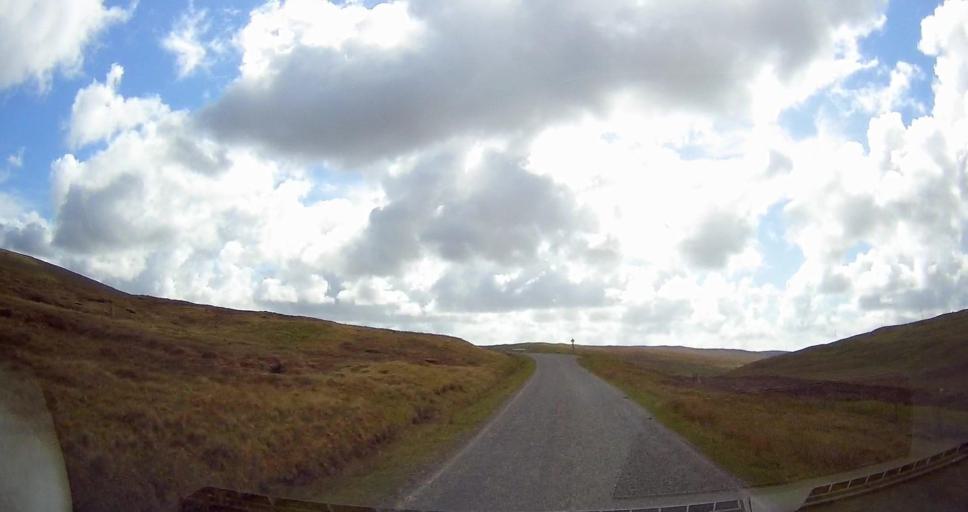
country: GB
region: Scotland
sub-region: Shetland Islands
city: Lerwick
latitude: 60.5158
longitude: -1.3794
